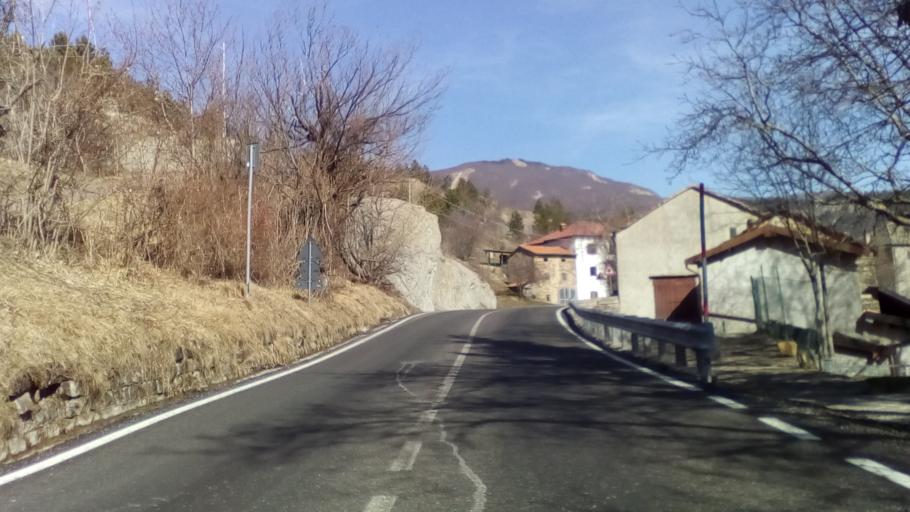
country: IT
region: Emilia-Romagna
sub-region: Provincia di Modena
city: Riolunato
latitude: 44.2458
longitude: 10.6331
